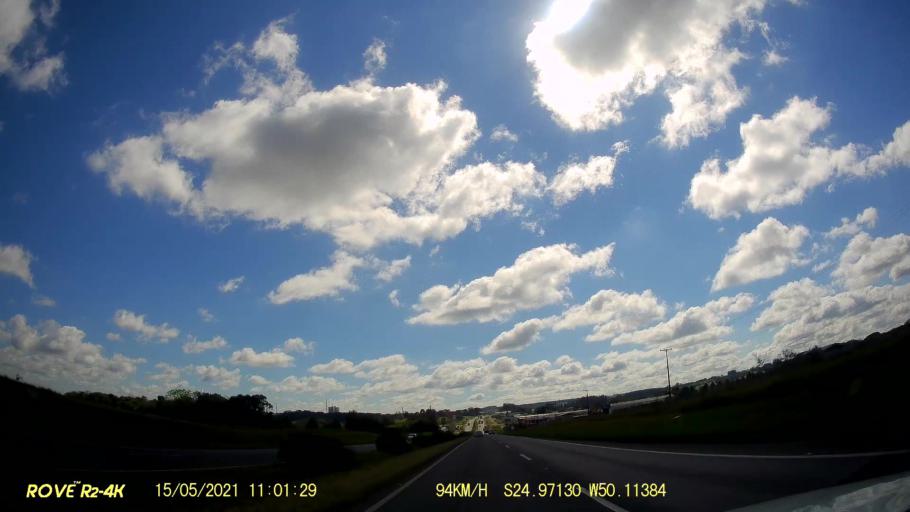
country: BR
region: Parana
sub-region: Carambei
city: Carambei
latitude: -24.9713
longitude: -50.1137
